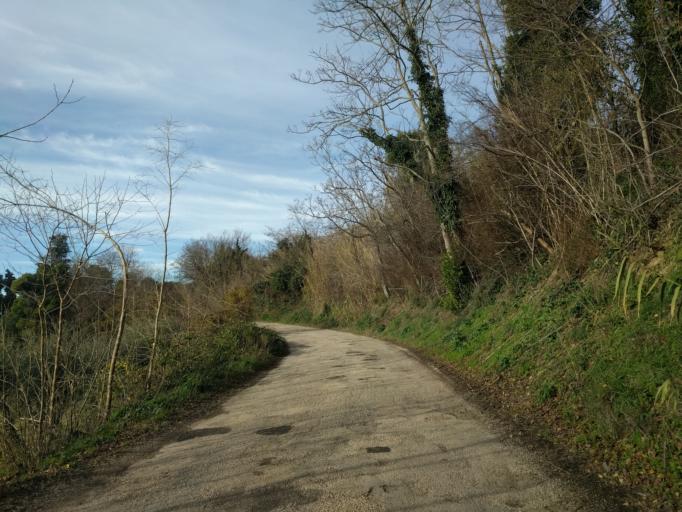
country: IT
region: The Marches
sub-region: Provincia di Pesaro e Urbino
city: Cuccurano
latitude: 43.8077
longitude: 12.9535
